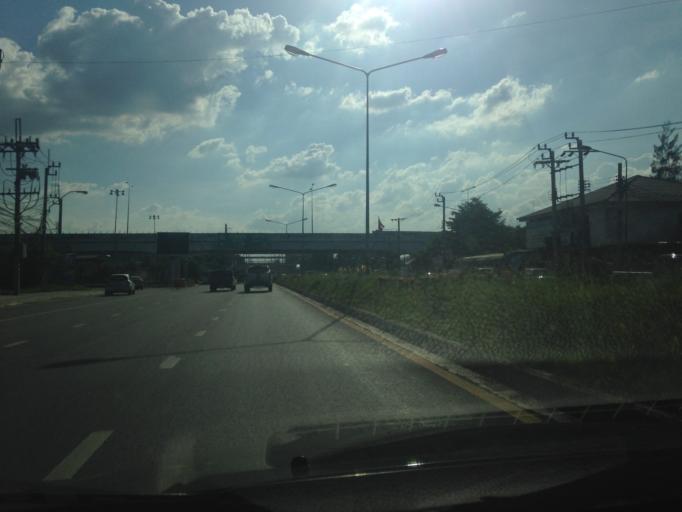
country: TH
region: Nonthaburi
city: Pak Kret
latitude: 13.9229
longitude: 100.5223
